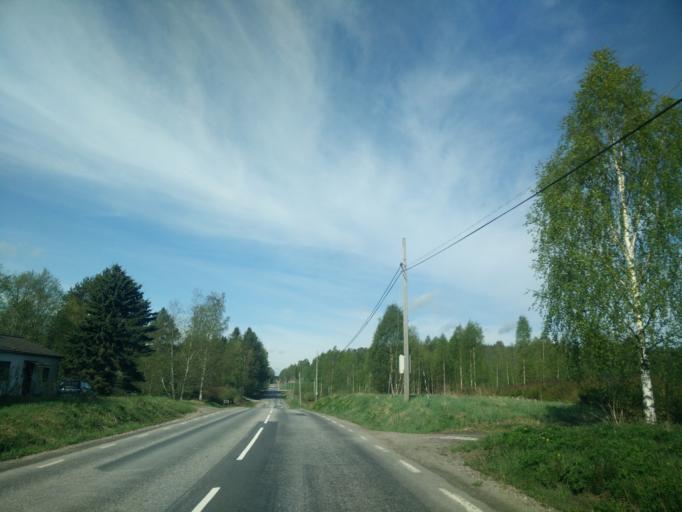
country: SE
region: Vaesternorrland
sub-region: Sundsvalls Kommun
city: Vi
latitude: 62.3102
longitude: 17.2400
